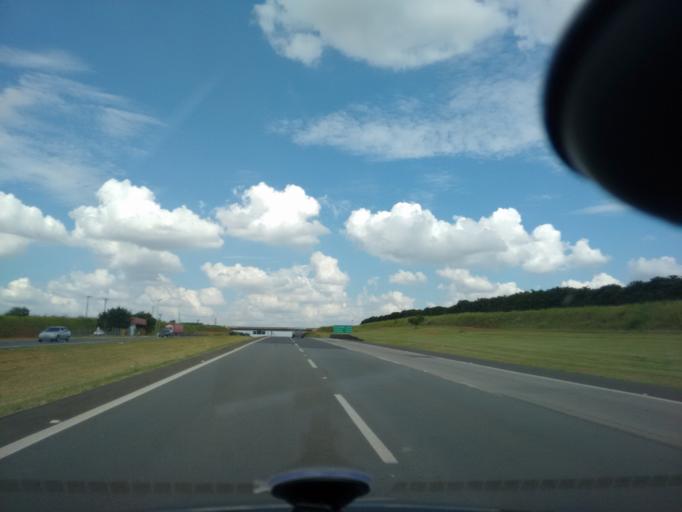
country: BR
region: Sao Paulo
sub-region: Sumare
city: Sumare
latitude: -22.8631
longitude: -47.2847
